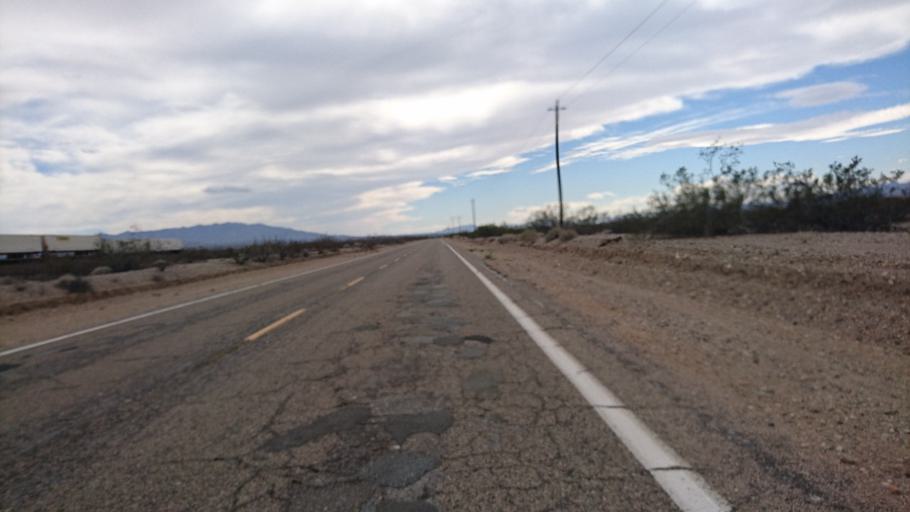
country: US
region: California
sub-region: San Bernardino County
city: Needles
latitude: 34.7798
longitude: -115.2076
